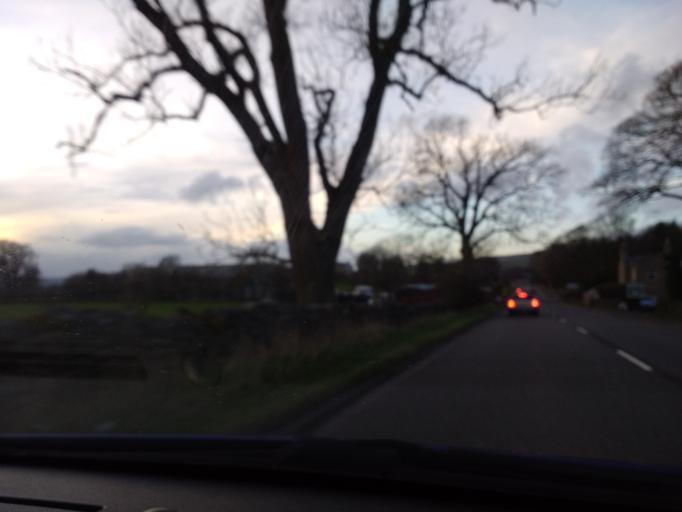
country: GB
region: England
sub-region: North Yorkshire
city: Ingleton
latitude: 54.1403
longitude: -2.4616
